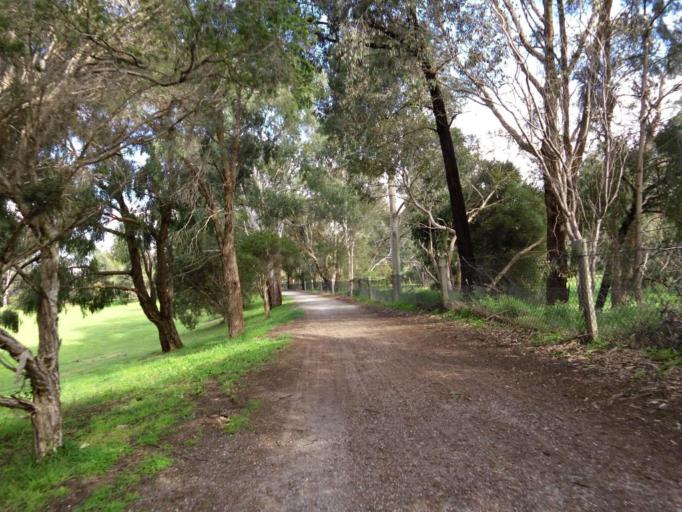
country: AU
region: Victoria
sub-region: Banyule
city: Viewbank
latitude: -37.7482
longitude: 145.0875
